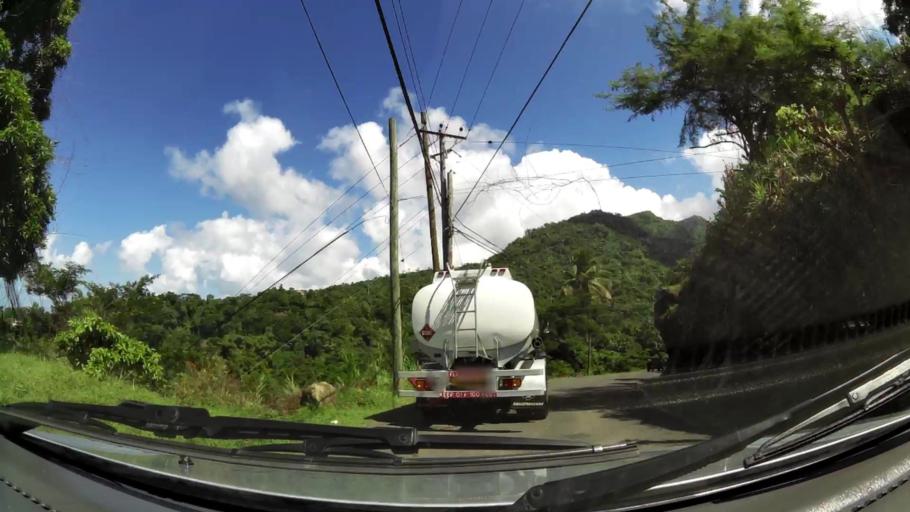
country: GD
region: Saint John
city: Gouyave
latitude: 12.1167
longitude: -61.7439
